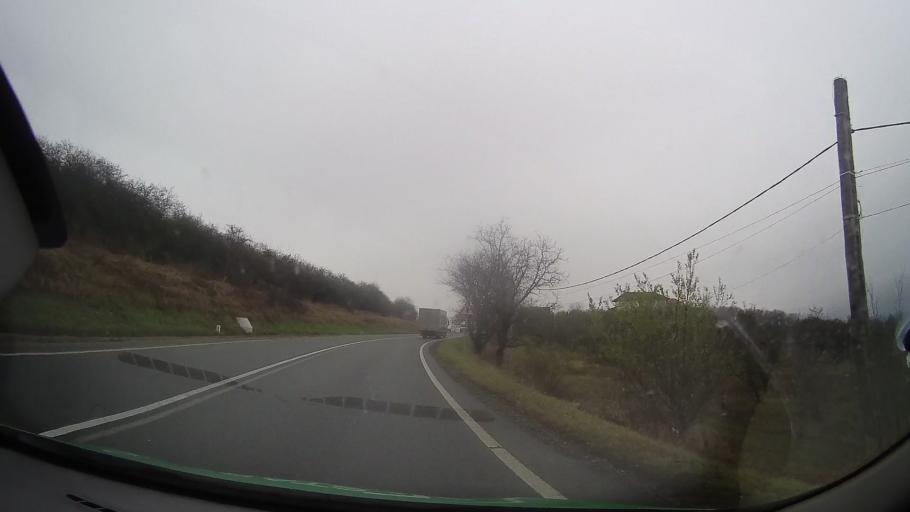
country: RO
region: Mures
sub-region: Comuna Breaza
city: Breaza
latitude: 46.7657
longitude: 24.6592
